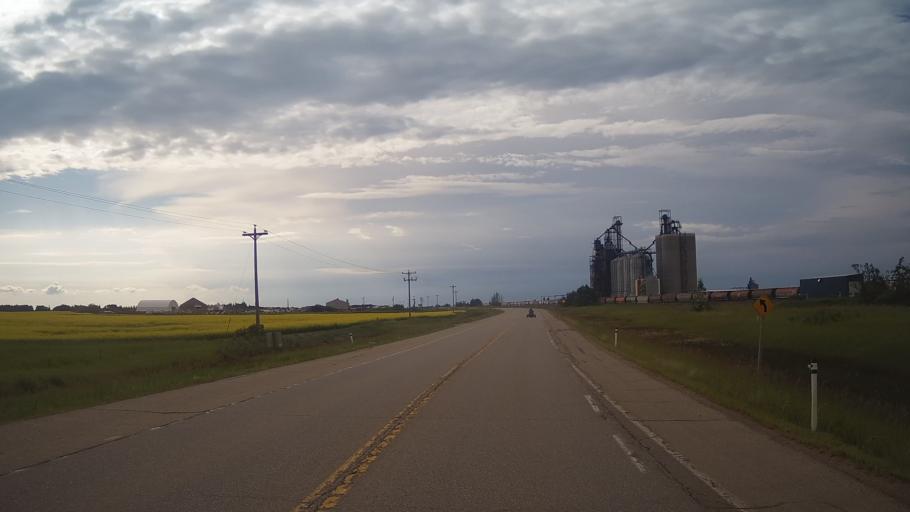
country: CA
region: Alberta
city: Viking
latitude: 53.0959
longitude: -111.7906
